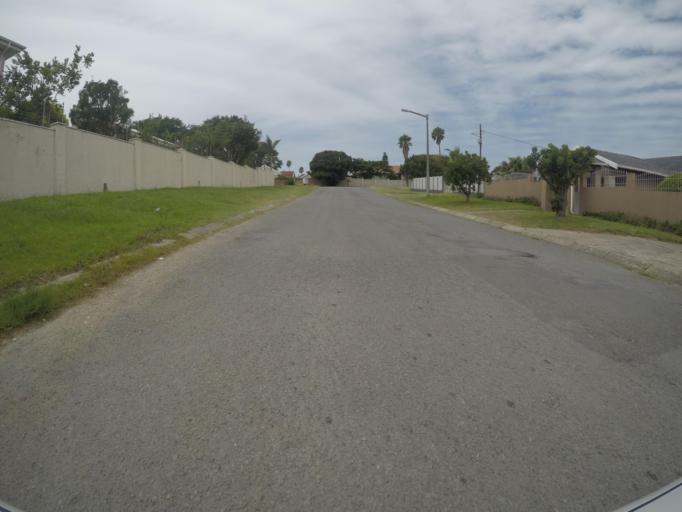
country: ZA
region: Eastern Cape
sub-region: Buffalo City Metropolitan Municipality
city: East London
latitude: -32.9605
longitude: 27.9326
